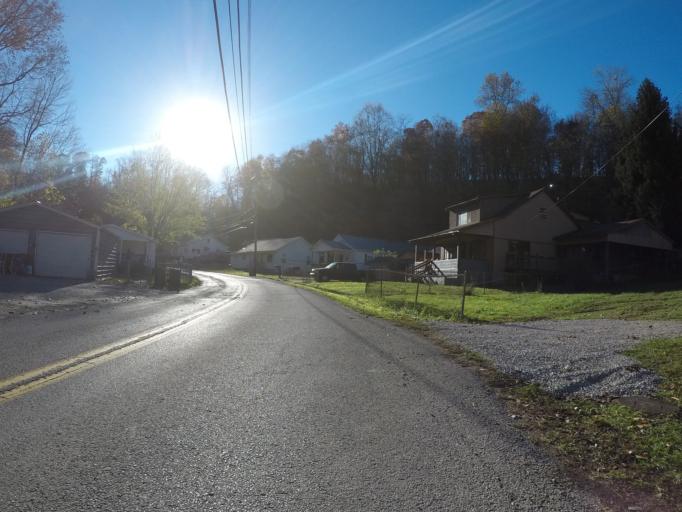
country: US
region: West Virginia
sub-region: Wayne County
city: Kenova
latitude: 38.3905
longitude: -82.5702
